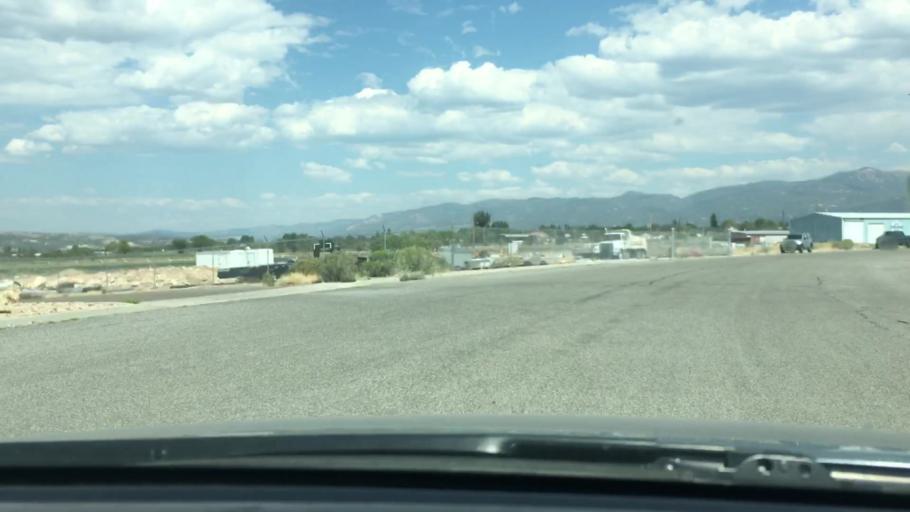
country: US
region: Utah
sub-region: Sanpete County
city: Mount Pleasant
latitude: 39.5303
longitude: -111.4692
